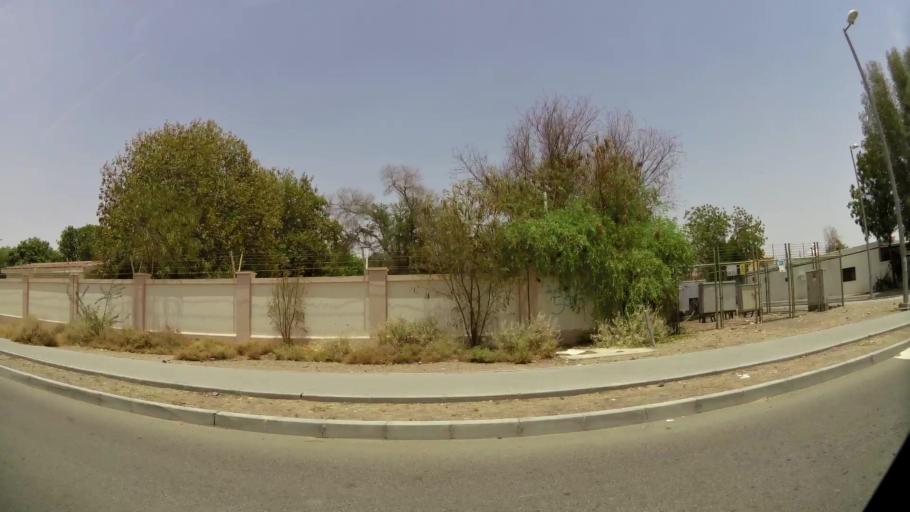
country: AE
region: Abu Dhabi
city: Al Ain
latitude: 24.2192
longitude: 55.7188
